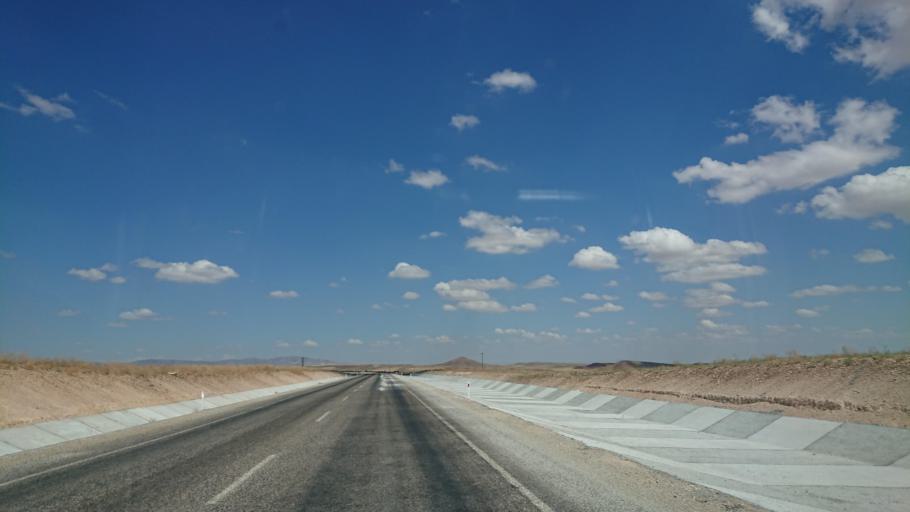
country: TR
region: Kirsehir
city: Kirsehir
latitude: 39.1226
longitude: 34.0031
